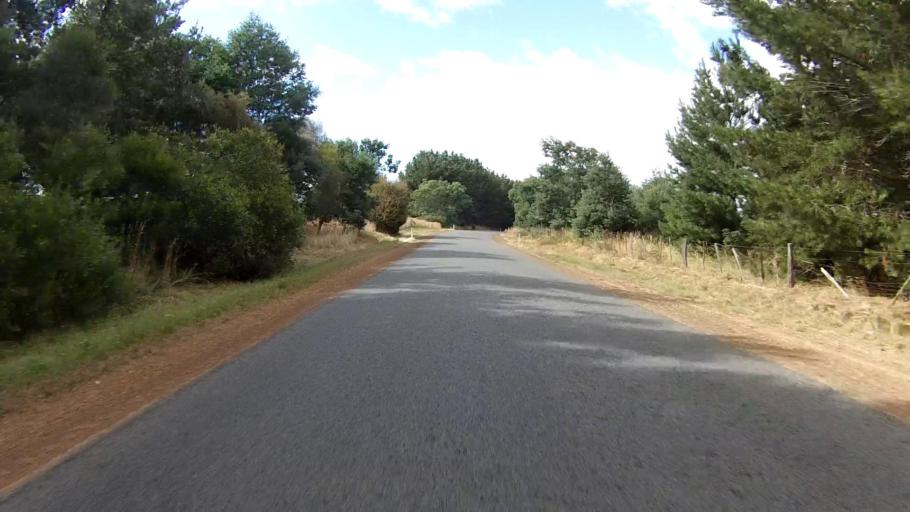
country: AU
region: Tasmania
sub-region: Northern Midlands
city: Evandale
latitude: -41.6927
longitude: 147.3654
